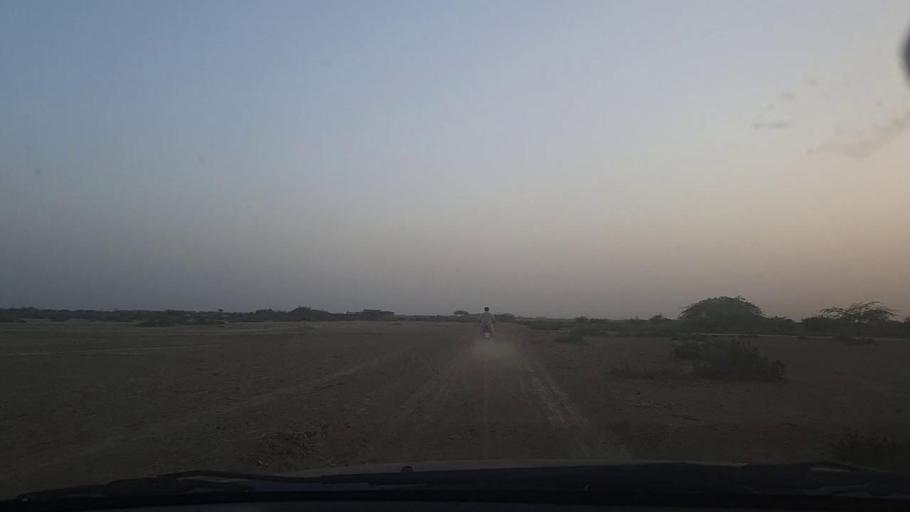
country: PK
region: Sindh
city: Mirpur Sakro
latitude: 24.3795
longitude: 67.6541
